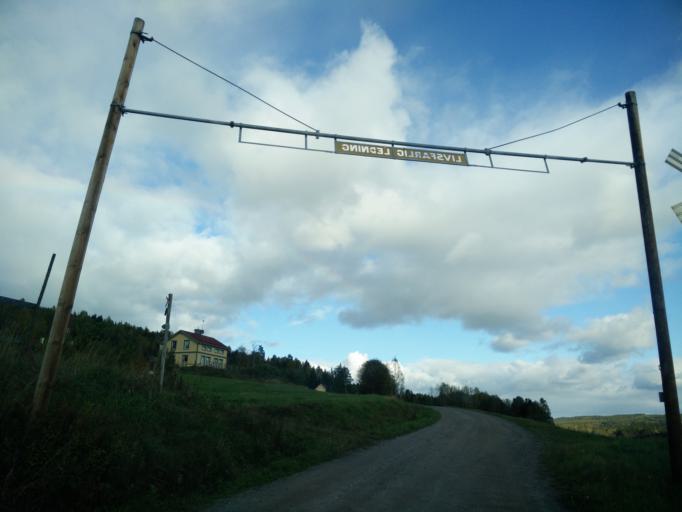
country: SE
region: Vaesternorrland
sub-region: Sundsvalls Kommun
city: Matfors
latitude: 62.3642
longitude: 17.0628
